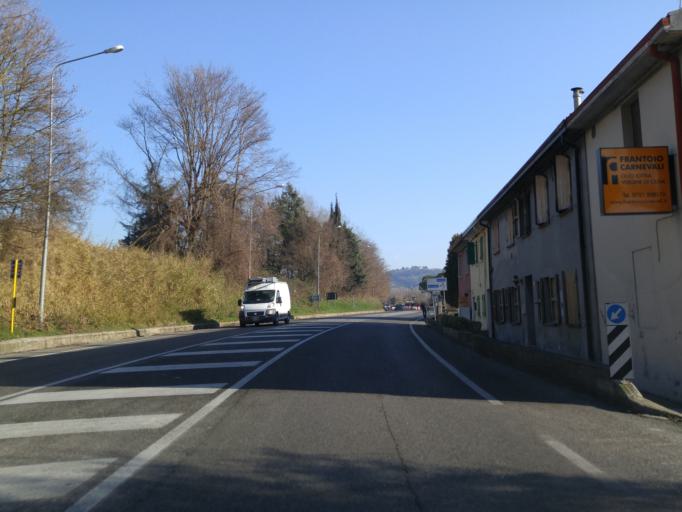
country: IT
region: The Marches
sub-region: Provincia di Pesaro e Urbino
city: Gradara
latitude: 43.9485
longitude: 12.7926
